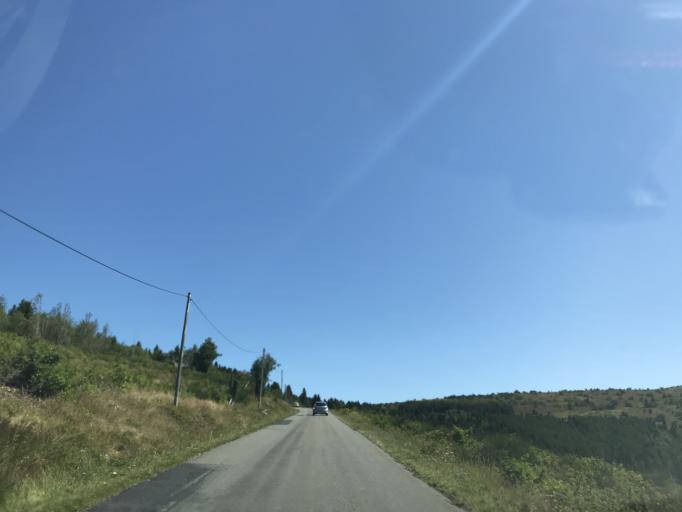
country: FR
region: Auvergne
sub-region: Departement du Puy-de-Dome
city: Job
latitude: 45.6836
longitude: 3.7731
